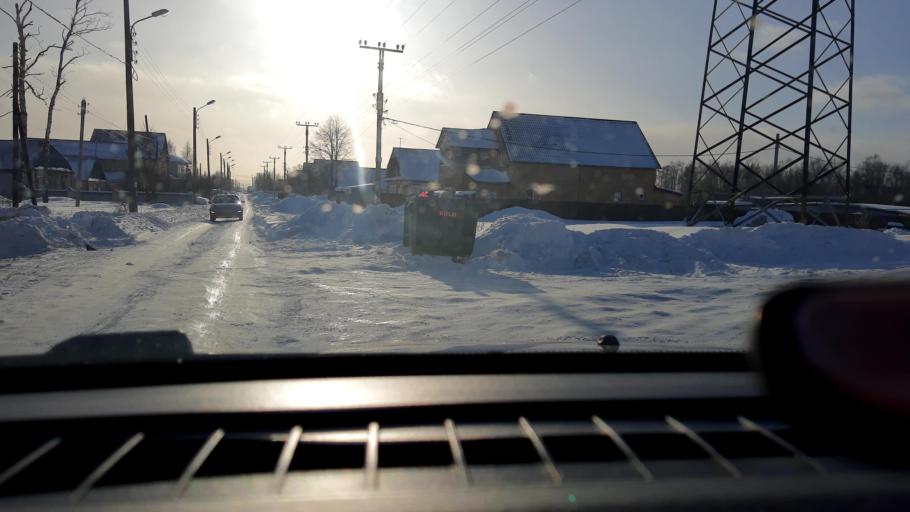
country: RU
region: Nizjnij Novgorod
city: Nizhniy Novgorod
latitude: 56.2113
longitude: 43.9568
